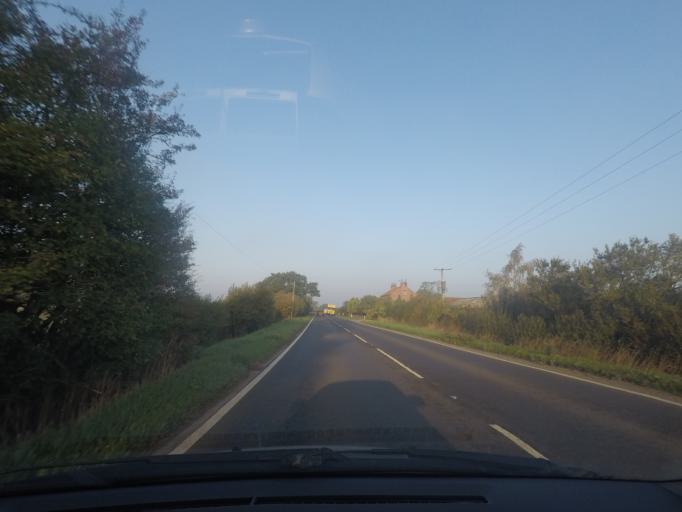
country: GB
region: England
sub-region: City of York
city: Askham Richard
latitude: 53.9930
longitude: -1.2416
